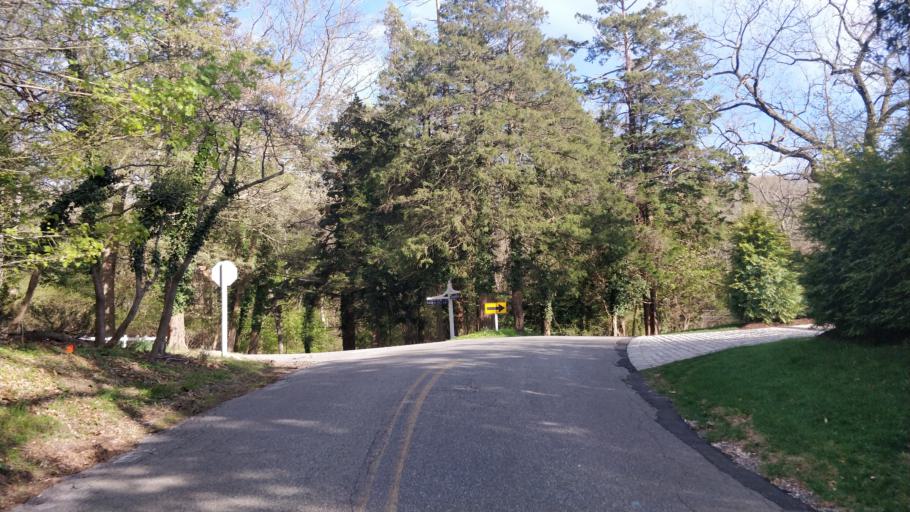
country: US
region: New York
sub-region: Suffolk County
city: Head of the Harbor
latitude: 40.8998
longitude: -73.1674
